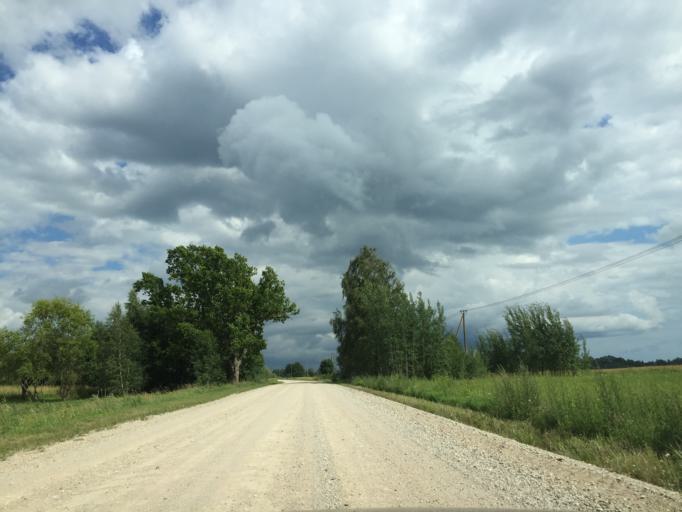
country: LV
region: Malpils
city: Malpils
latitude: 56.8550
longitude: 25.0404
